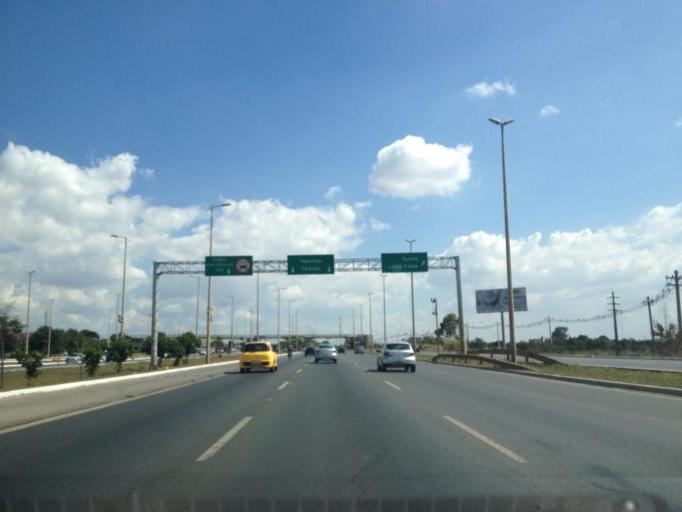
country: BR
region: Federal District
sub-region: Brasilia
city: Brasilia
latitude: -15.8092
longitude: -47.9738
